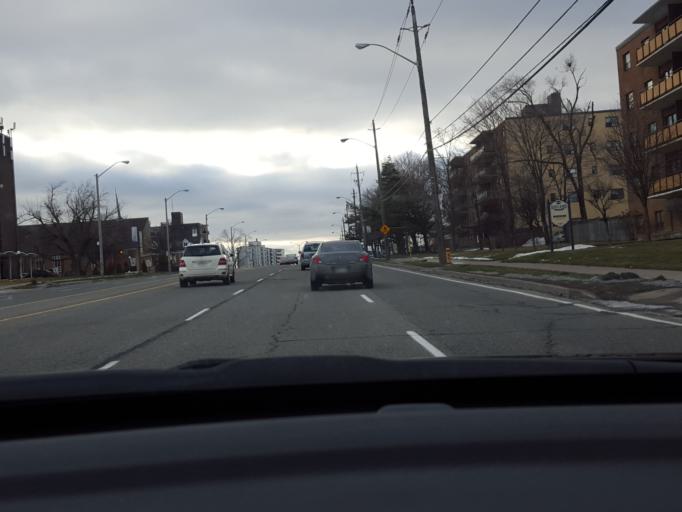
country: CA
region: Ontario
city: Scarborough
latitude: 43.7432
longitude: -79.3052
